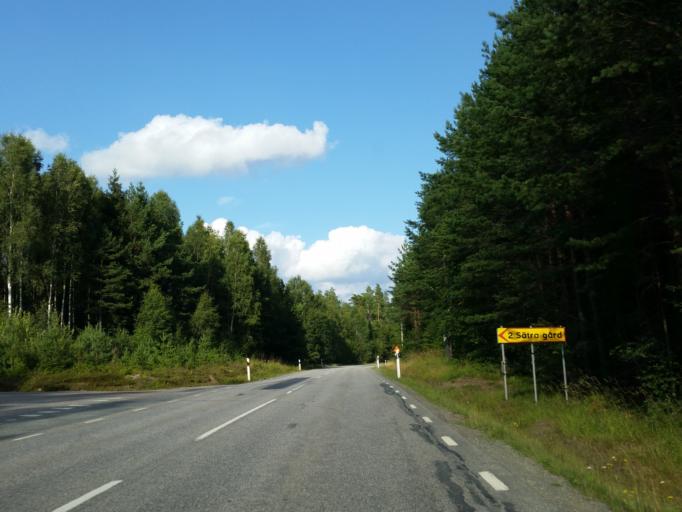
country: SE
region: Stockholm
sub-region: Nykvarns Kommun
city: Nykvarn
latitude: 59.2075
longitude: 17.3758
